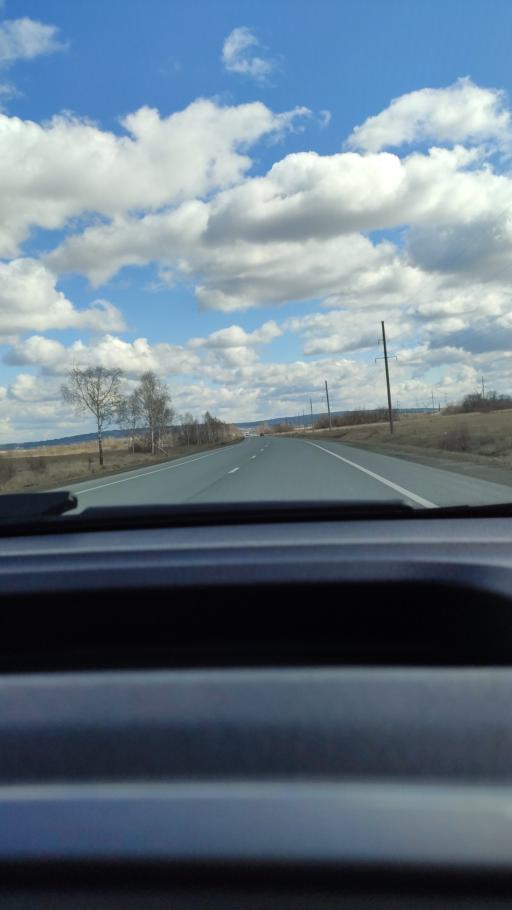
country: RU
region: Samara
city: Kurumoch
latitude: 53.4911
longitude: 49.9763
